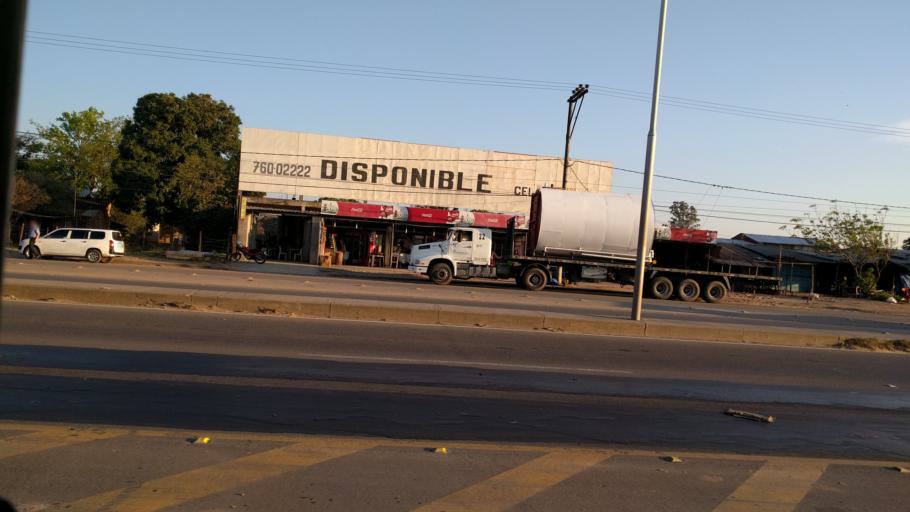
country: BO
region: Santa Cruz
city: Cotoca
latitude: -17.7654
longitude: -63.0864
